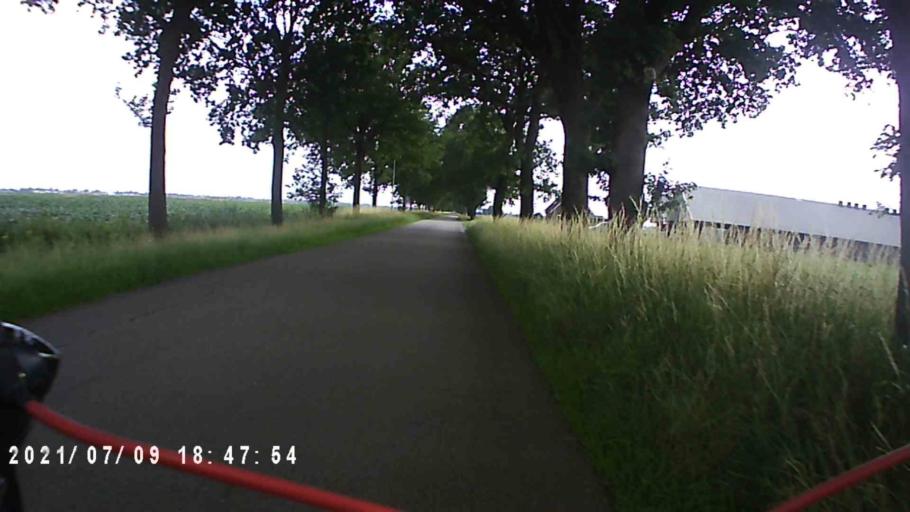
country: NL
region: Groningen
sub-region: Gemeente Veendam
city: Veendam
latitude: 53.0679
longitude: 6.9170
